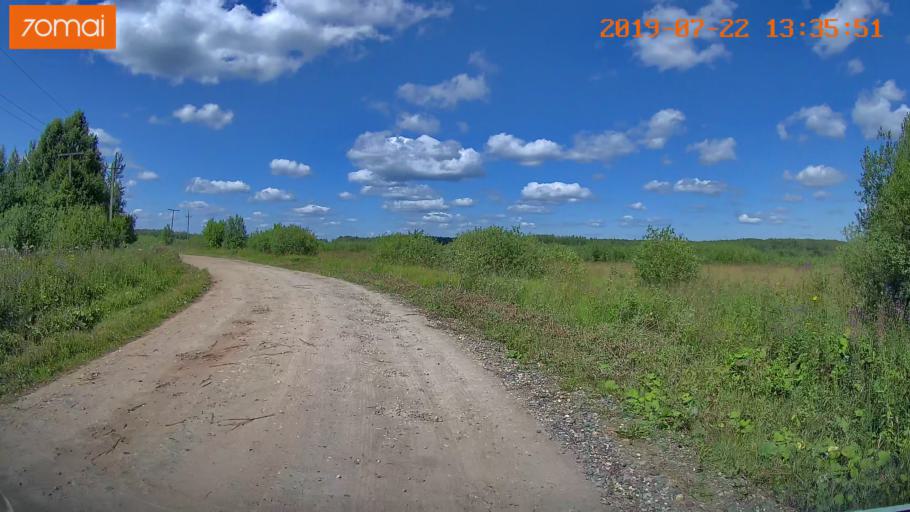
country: RU
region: Ivanovo
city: Novo-Talitsy
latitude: 57.0651
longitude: 40.8937
